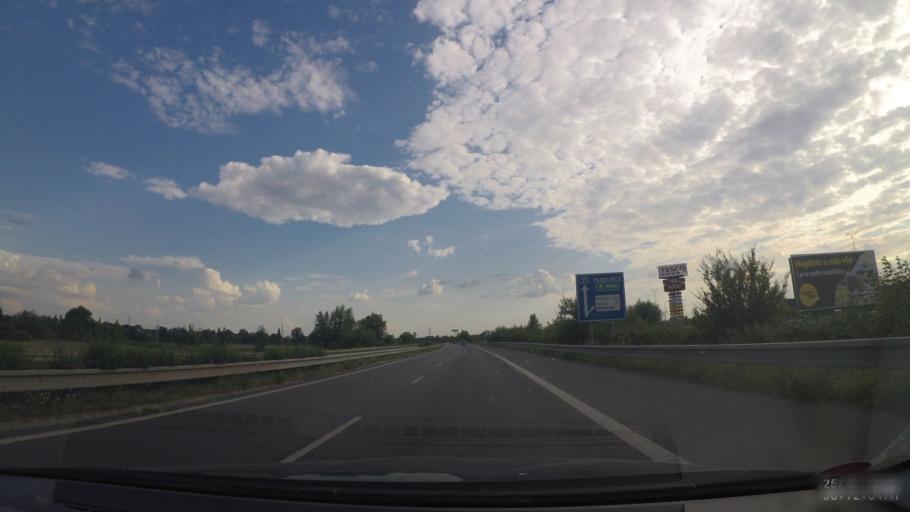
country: CZ
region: Kralovehradecky
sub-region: Okres Hradec Kralove
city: Hradec Kralove
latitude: 50.1903
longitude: 15.8075
